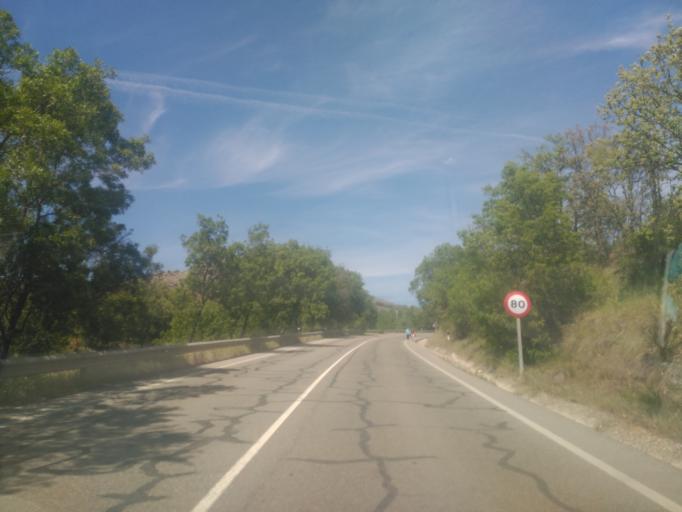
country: ES
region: Castille and Leon
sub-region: Provincia de Salamanca
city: Bejar
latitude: 40.3939
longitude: -5.7401
